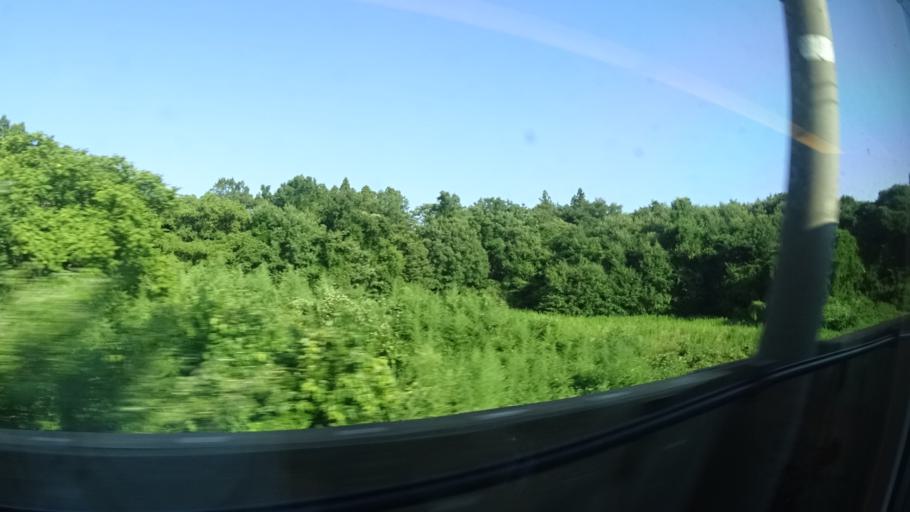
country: JP
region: Fukushima
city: Motomiya
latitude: 37.4823
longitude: 140.4184
